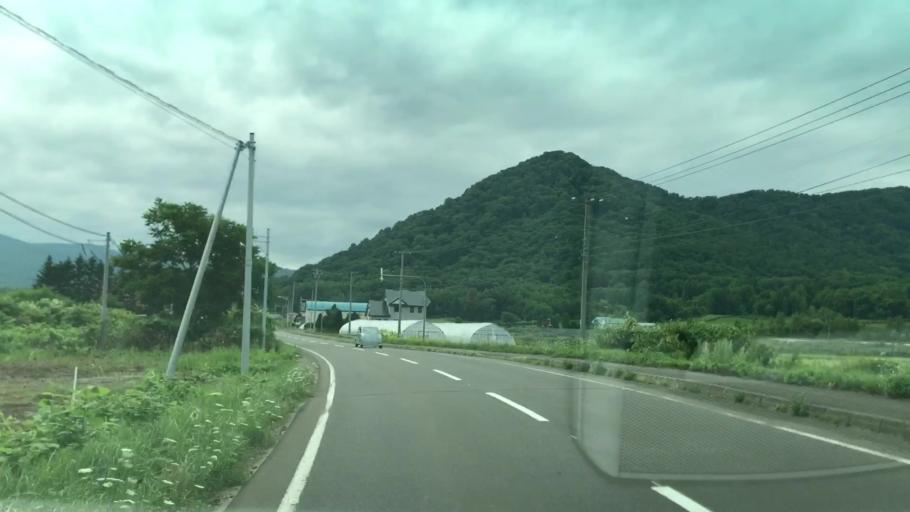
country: JP
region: Hokkaido
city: Yoichi
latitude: 43.0781
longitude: 140.8162
